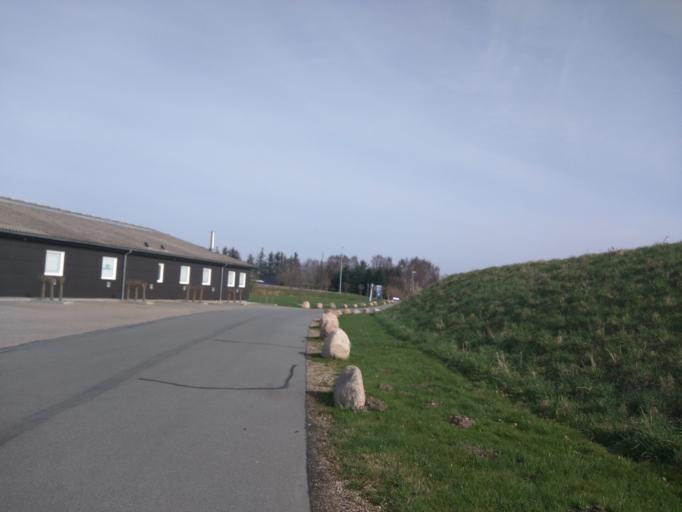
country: DK
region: South Denmark
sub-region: Fredericia Kommune
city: Snoghoj
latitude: 55.5376
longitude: 9.7085
